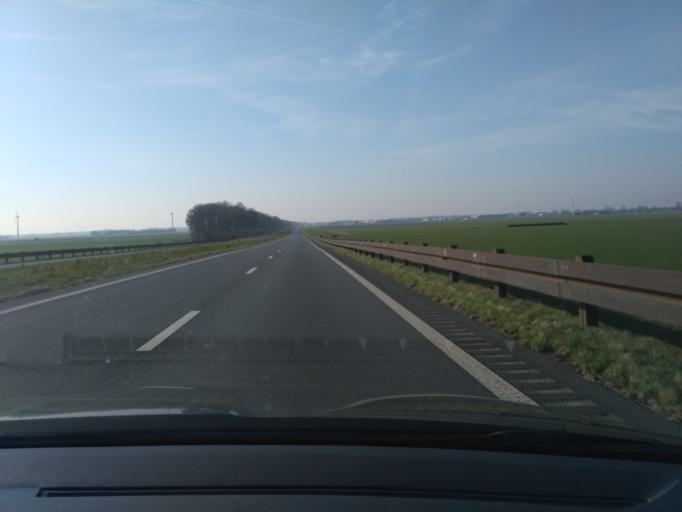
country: NL
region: Flevoland
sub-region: Gemeente Zeewolde
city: Zeewolde
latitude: 52.3766
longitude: 5.5456
